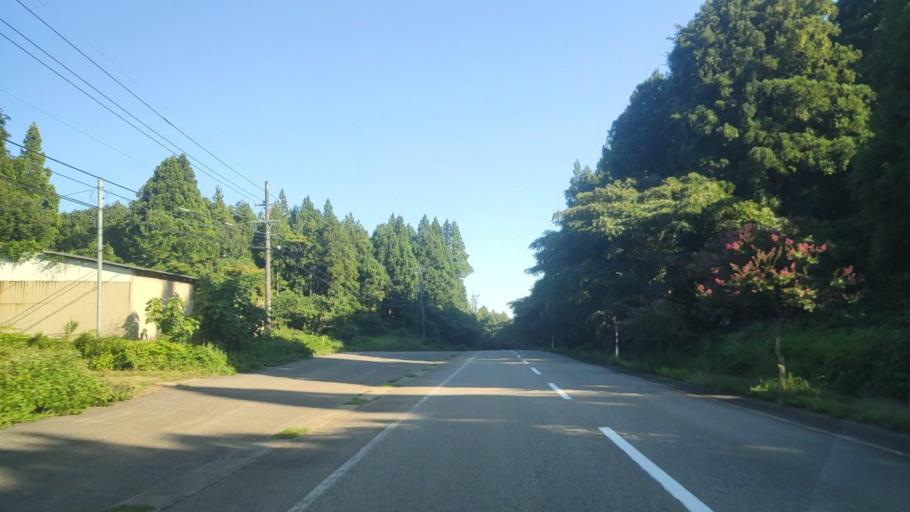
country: JP
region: Ishikawa
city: Nanao
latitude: 37.1268
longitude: 136.9245
